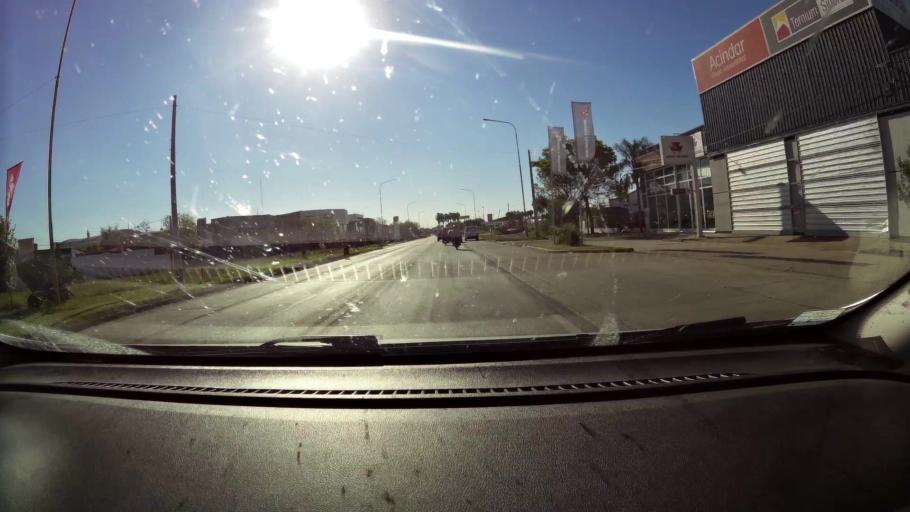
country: AR
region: Cordoba
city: San Francisco
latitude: -31.4156
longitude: -62.0894
